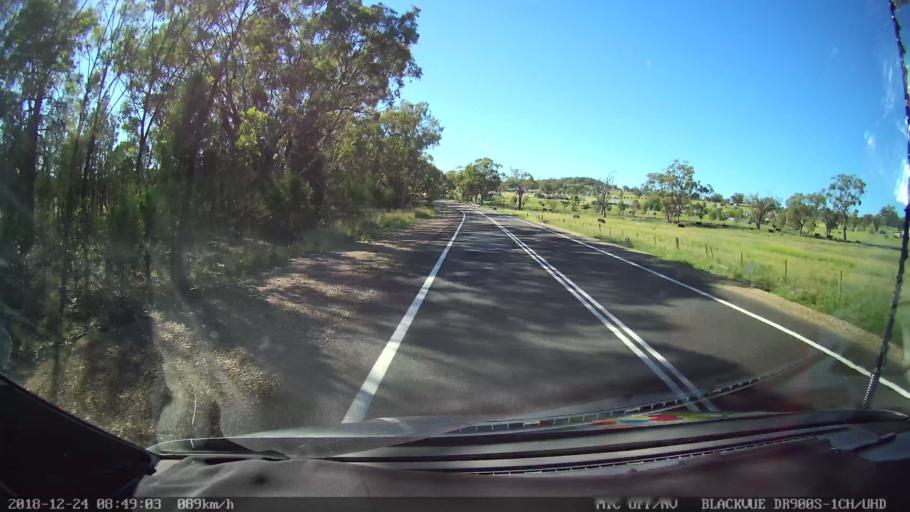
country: AU
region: New South Wales
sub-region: Liverpool Plains
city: Quirindi
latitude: -31.4630
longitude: 150.6503
